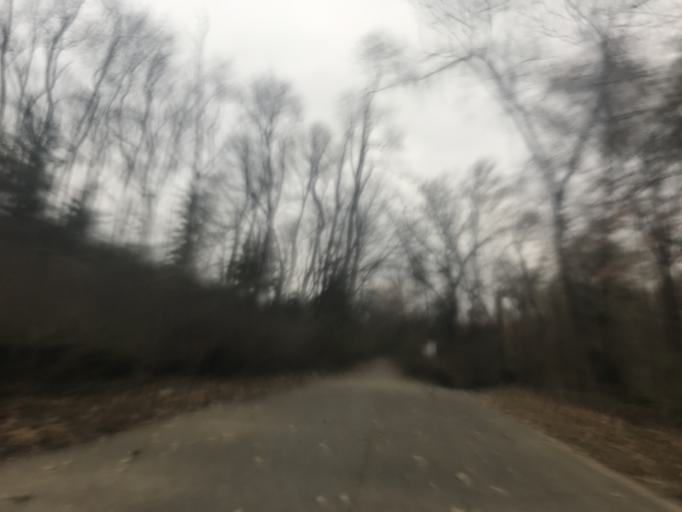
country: US
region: Indiana
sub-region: Clark County
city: Jeffersonville
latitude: 38.2649
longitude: -85.7205
